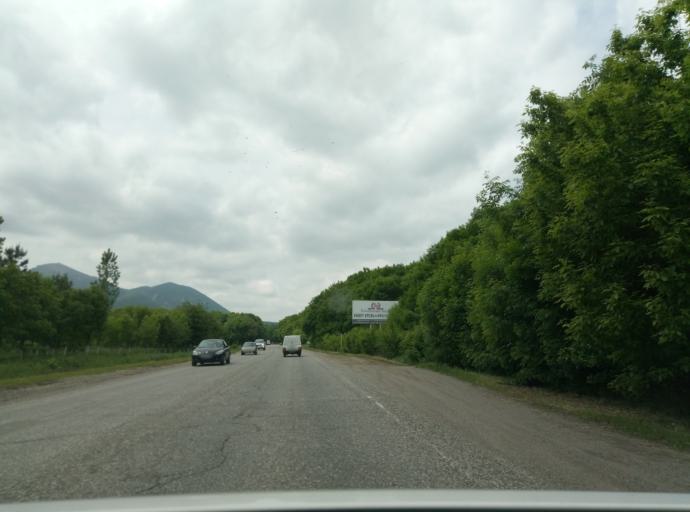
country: RU
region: Stavropol'skiy
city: Novoterskiy
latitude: 44.1275
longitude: 43.0820
